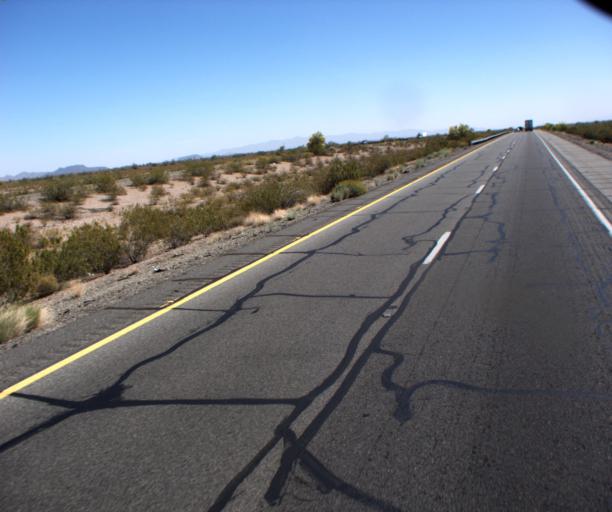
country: US
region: Arizona
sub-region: Maricopa County
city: Buckeye
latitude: 33.5137
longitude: -113.0306
